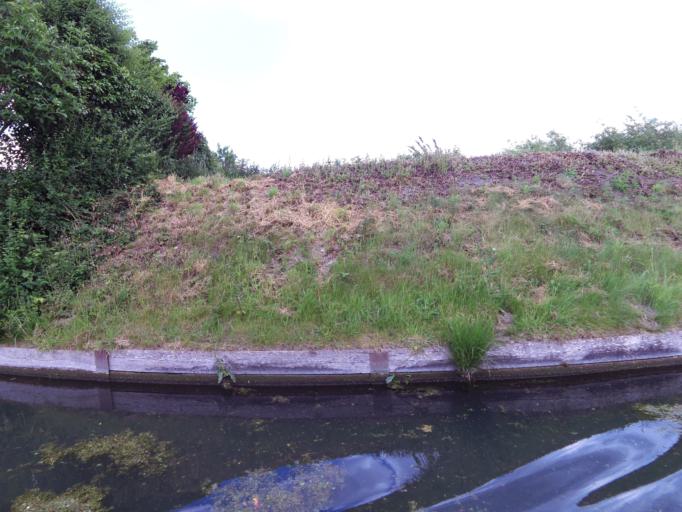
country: FR
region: Nord-Pas-de-Calais
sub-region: Departement du Pas-de-Calais
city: Saint-Omer
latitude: 50.7582
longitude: 2.2468
